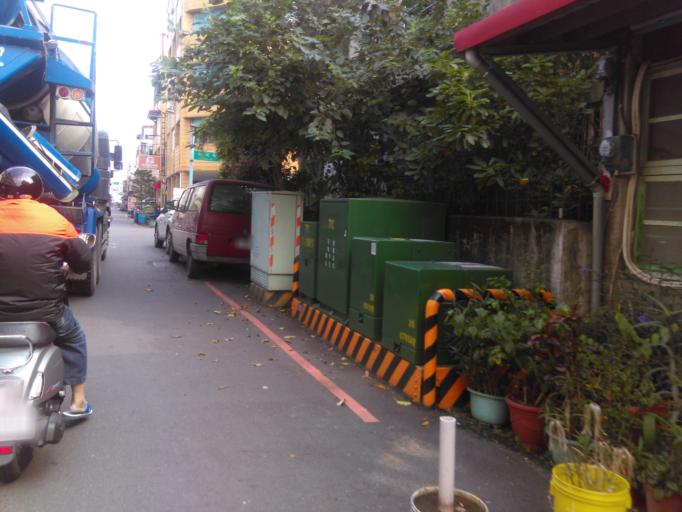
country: TW
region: Taiwan
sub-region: Yilan
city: Yilan
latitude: 24.7593
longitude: 121.7506
